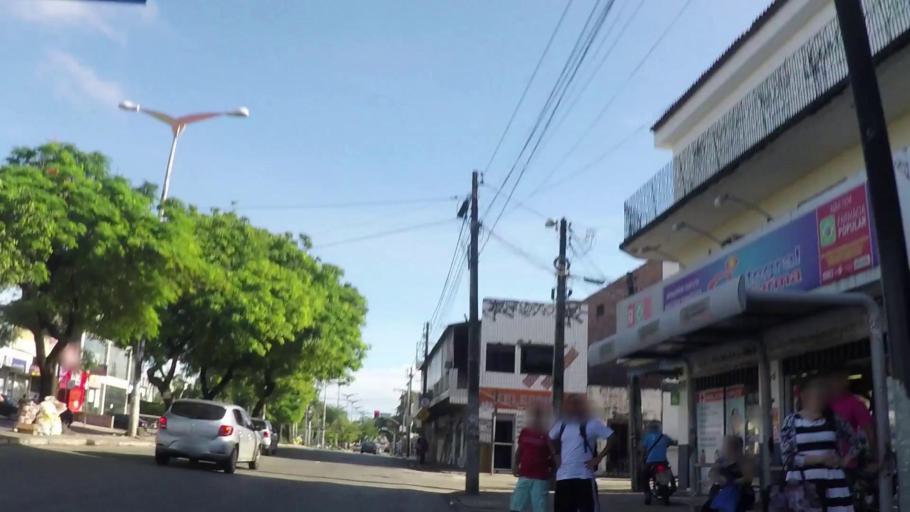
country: BR
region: Ceara
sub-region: Fortaleza
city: Fortaleza
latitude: -3.7347
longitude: -38.5841
